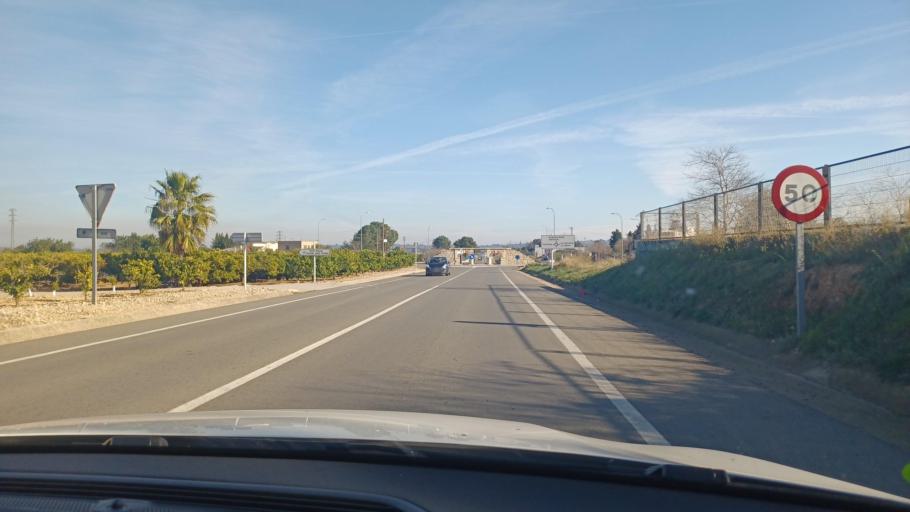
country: ES
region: Catalonia
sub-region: Provincia de Tarragona
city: Santa Barbara
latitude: 40.7167
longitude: 0.5037
